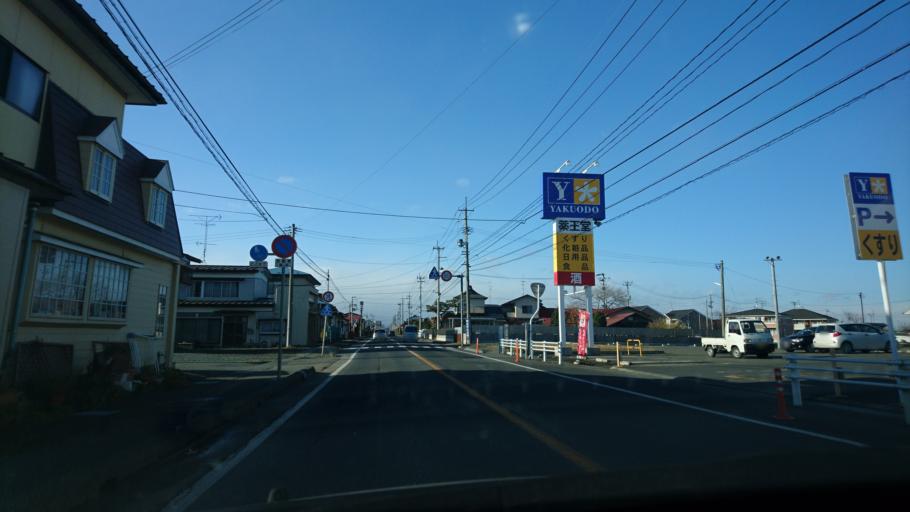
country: JP
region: Iwate
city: Mizusawa
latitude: 39.1262
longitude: 141.1612
